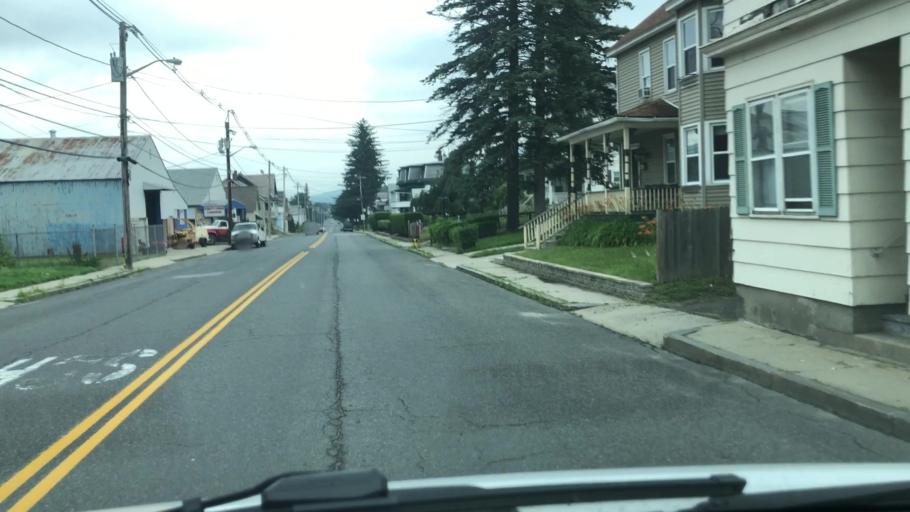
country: US
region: Massachusetts
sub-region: Berkshire County
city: Adams
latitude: 42.6258
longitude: -73.1128
